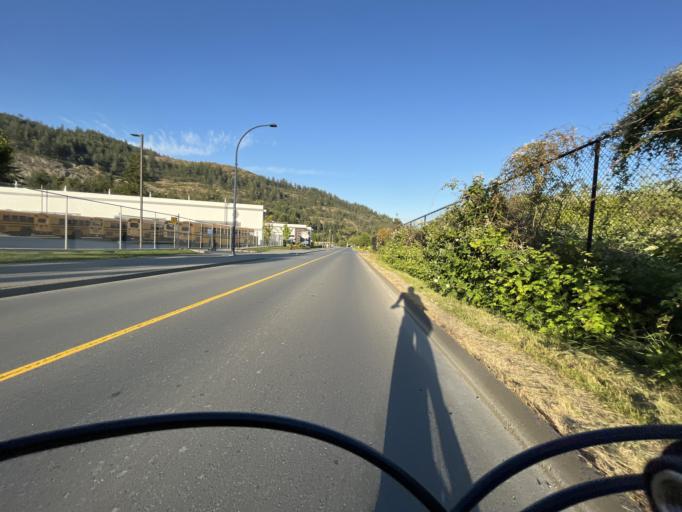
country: CA
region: British Columbia
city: Langford
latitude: 48.4581
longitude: -123.5438
